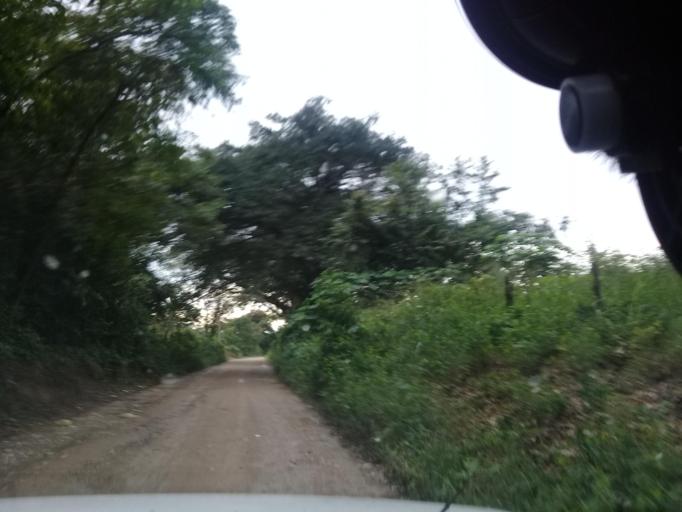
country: MX
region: Hidalgo
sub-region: Huejutla de Reyes
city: Chalahuiyapa
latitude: 21.1566
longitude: -98.3738
